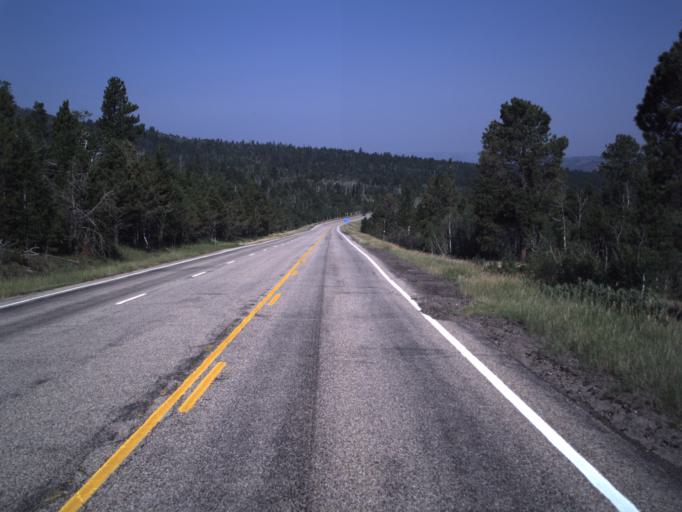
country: US
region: Utah
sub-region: Daggett County
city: Manila
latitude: 40.8612
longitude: -109.4725
